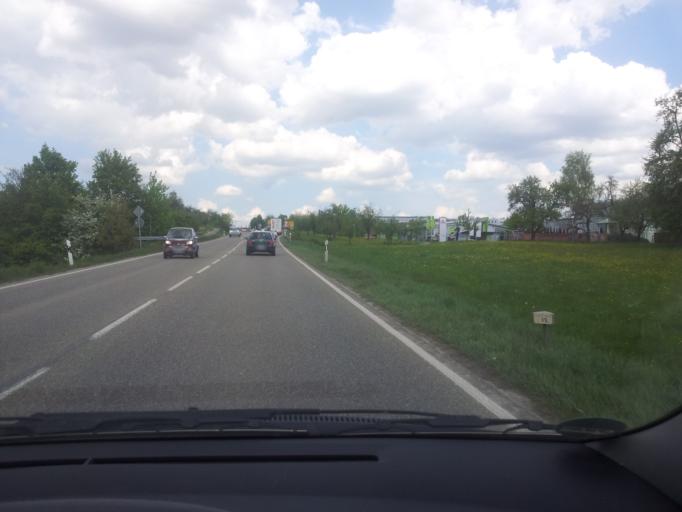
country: DE
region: Baden-Wuerttemberg
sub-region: Regierungsbezirk Stuttgart
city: Backnang
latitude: 48.9303
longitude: 9.4376
